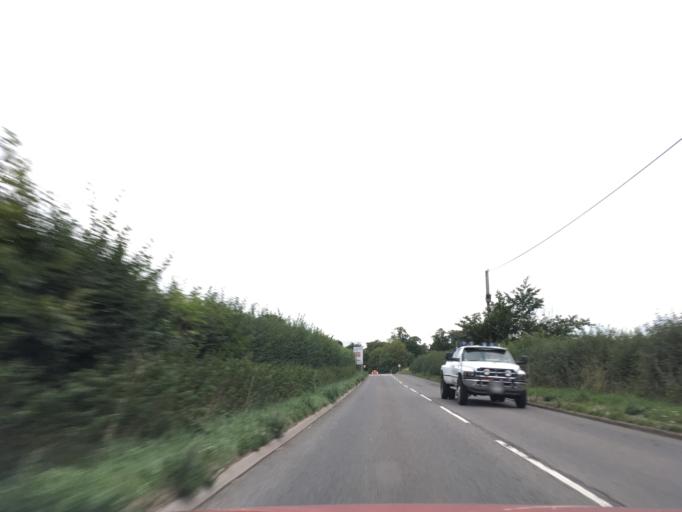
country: GB
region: England
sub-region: Wiltshire
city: Calne
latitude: 51.4003
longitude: -2.0465
